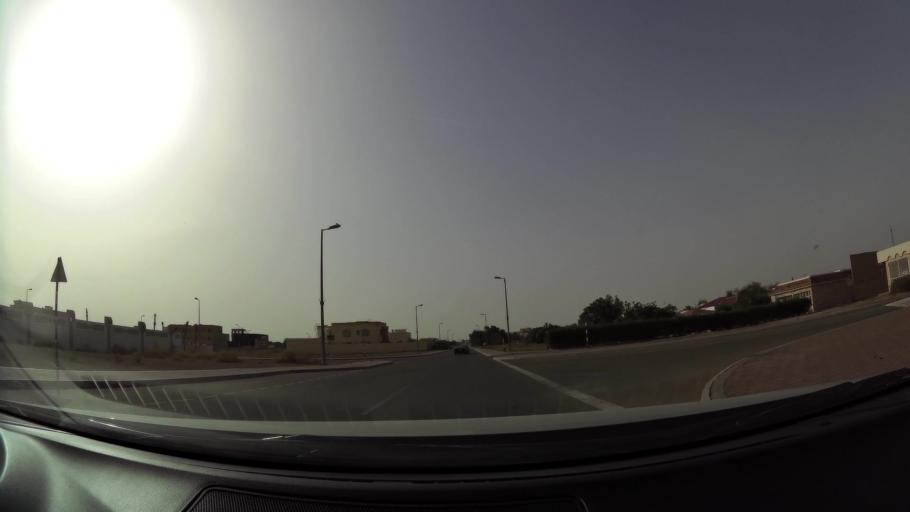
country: AE
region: Abu Dhabi
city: Al Ain
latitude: 24.1980
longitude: 55.6164
